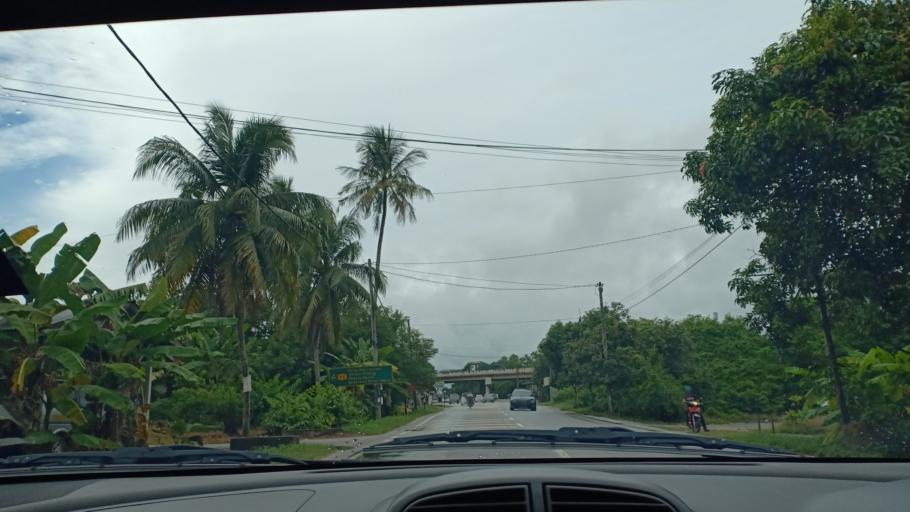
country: MY
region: Penang
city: Kepala Batas
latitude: 5.4972
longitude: 100.4377
